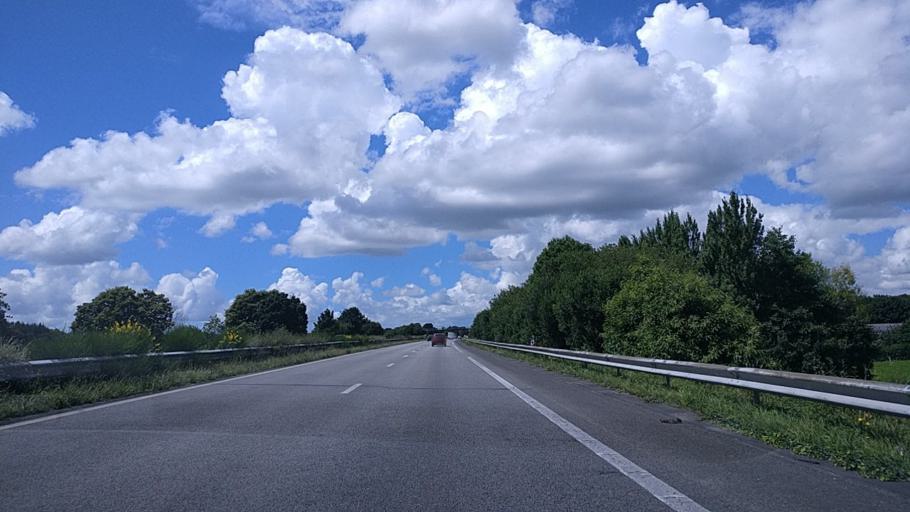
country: FR
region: Brittany
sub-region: Departement du Finistere
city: Saint-Yvi
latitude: 47.9439
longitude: -3.9304
